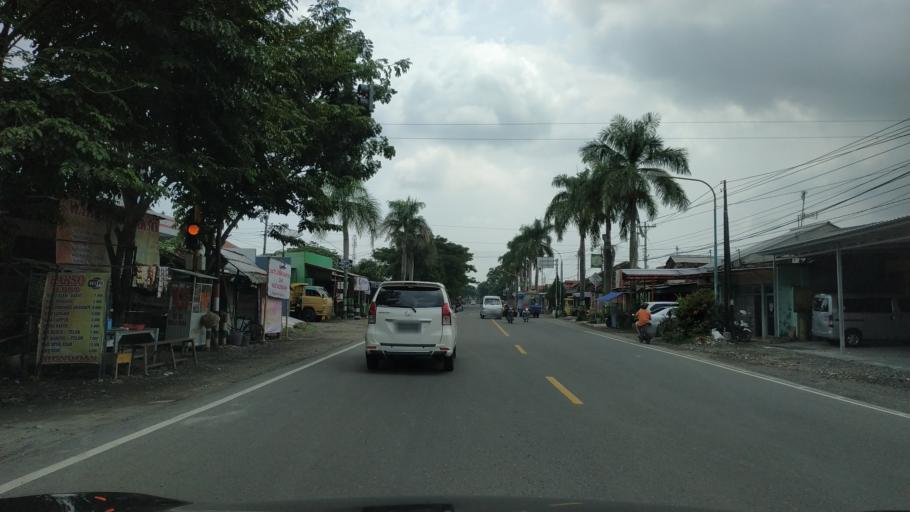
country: ID
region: Central Java
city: Slawi
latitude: -7.0057
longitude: 109.1405
